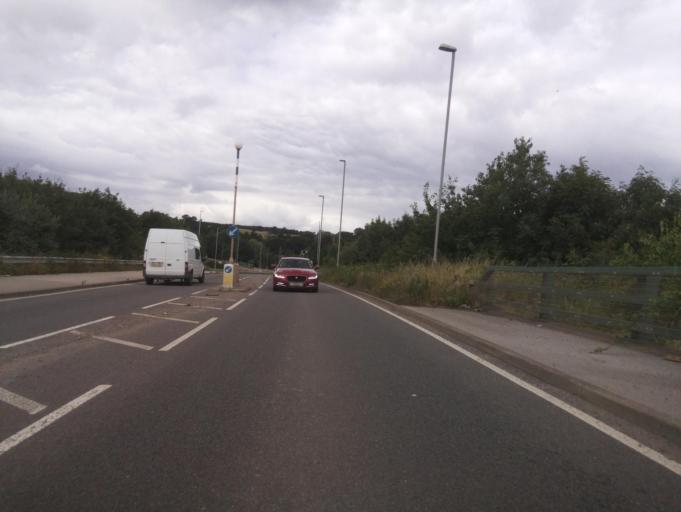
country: GB
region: England
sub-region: Nottinghamshire
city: Burton Joyce
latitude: 52.9749
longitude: -1.0596
